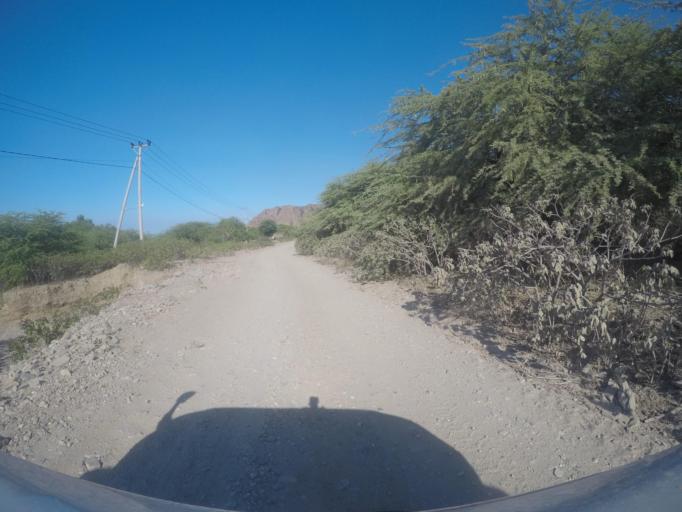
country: TL
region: Dili
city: Dili
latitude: -8.5278
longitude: 125.6319
